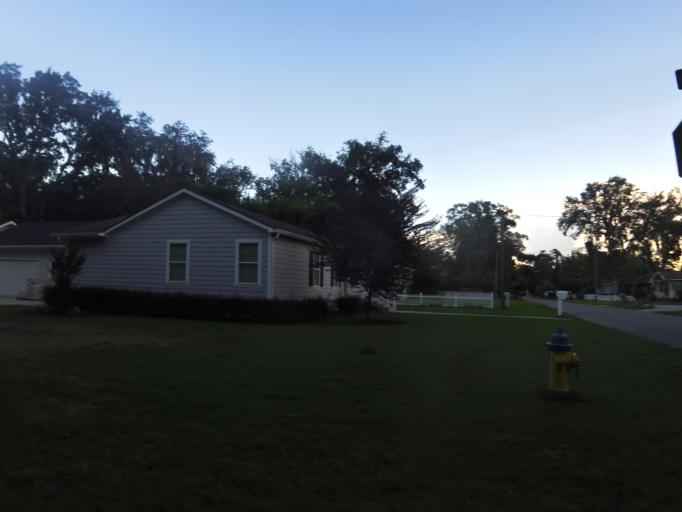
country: US
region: Georgia
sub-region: Camden County
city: St. Marys
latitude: 30.7350
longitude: -81.5557
